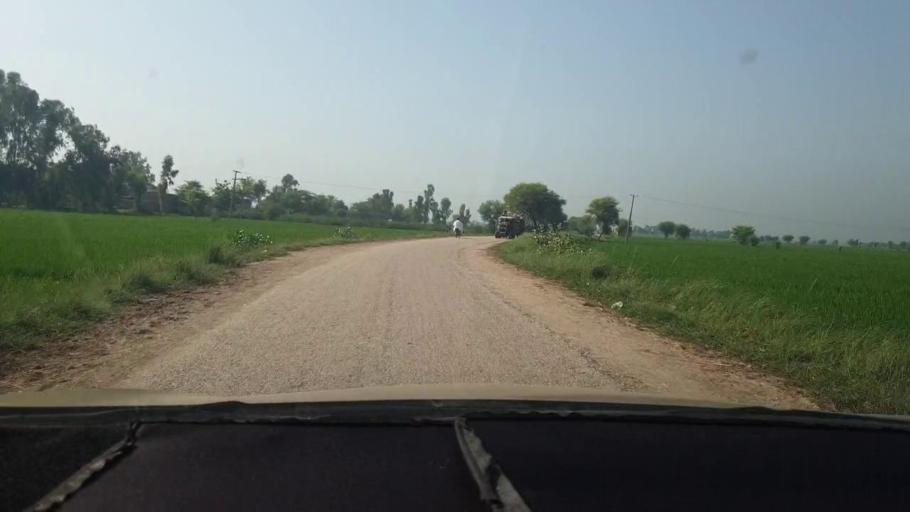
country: PK
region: Sindh
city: Kambar
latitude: 27.5996
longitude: 68.0936
